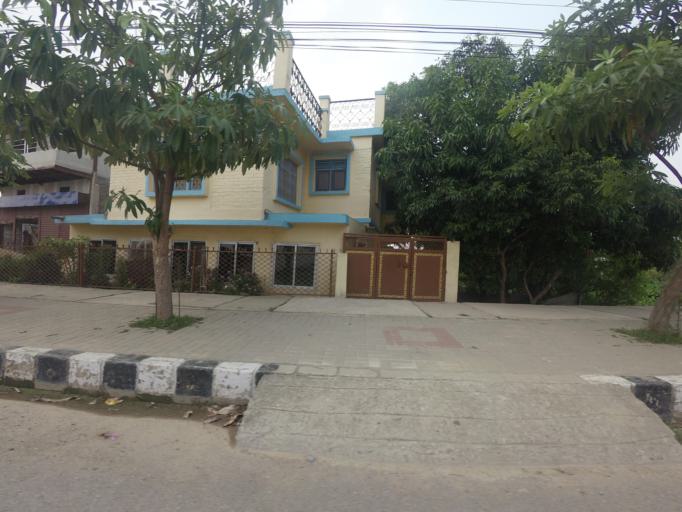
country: NP
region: Western Region
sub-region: Lumbini Zone
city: Bhairahawa
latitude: 27.5081
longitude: 83.4276
